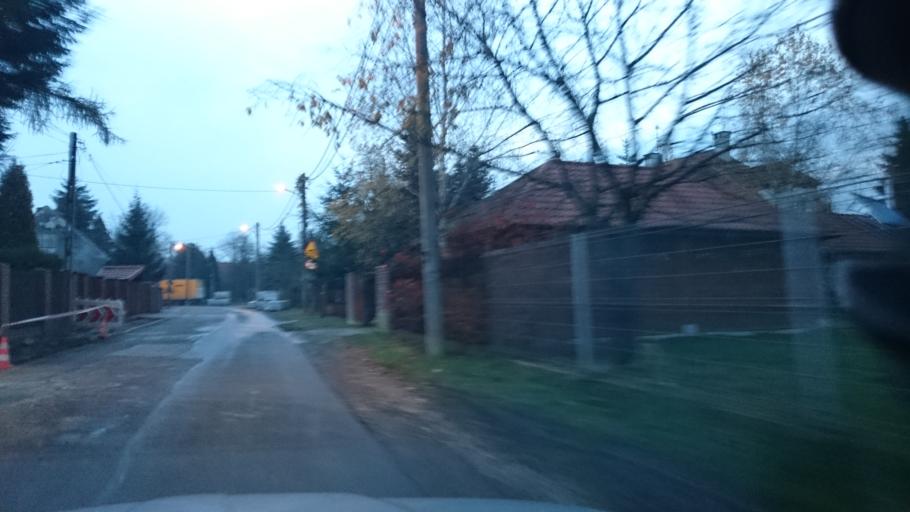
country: PL
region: Lesser Poland Voivodeship
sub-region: Powiat wielicki
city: Czarnochowice
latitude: 50.0163
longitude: 20.0337
